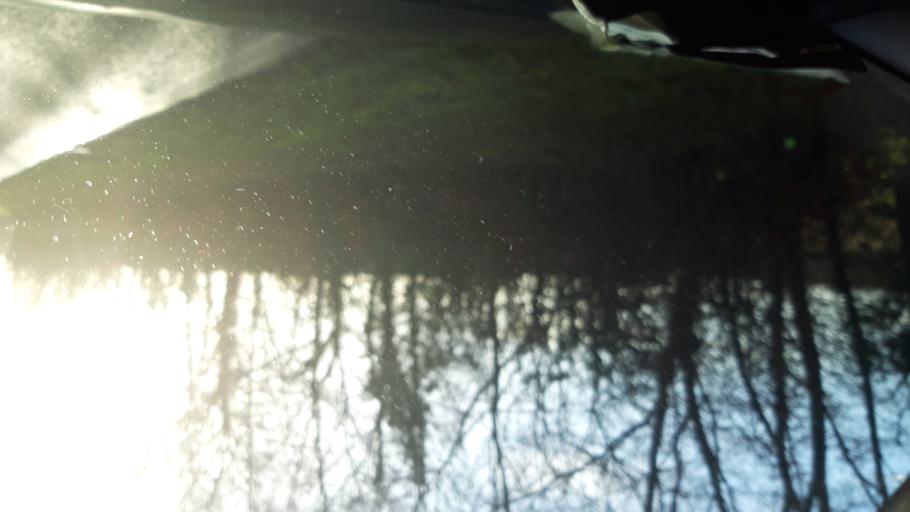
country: GB
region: Northern Ireland
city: Maghera
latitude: 54.8322
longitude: -6.6851
